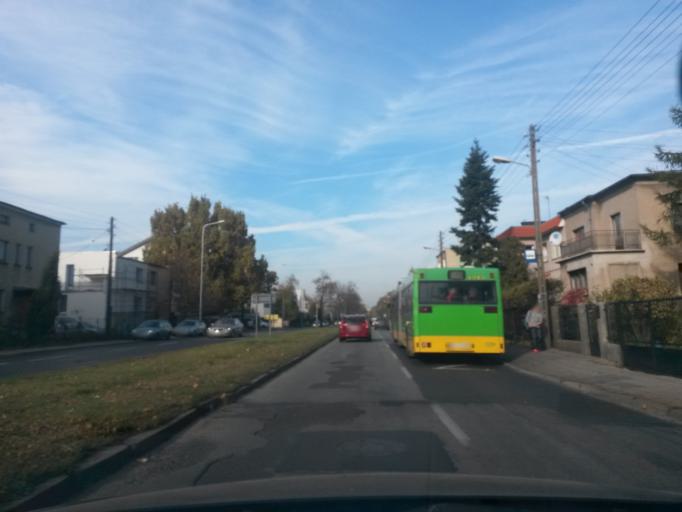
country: PL
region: Greater Poland Voivodeship
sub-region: Poznan
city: Poznan
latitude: 52.3960
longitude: 16.8813
